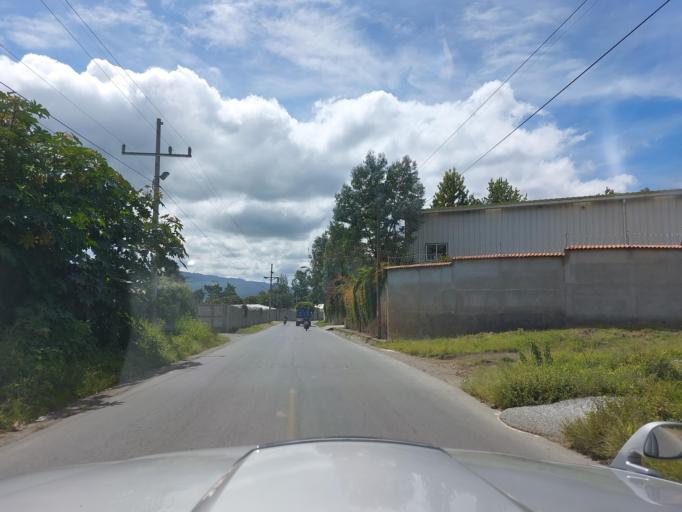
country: GT
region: Chimaltenango
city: San Andres Itzapa
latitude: 14.6168
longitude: -90.8259
